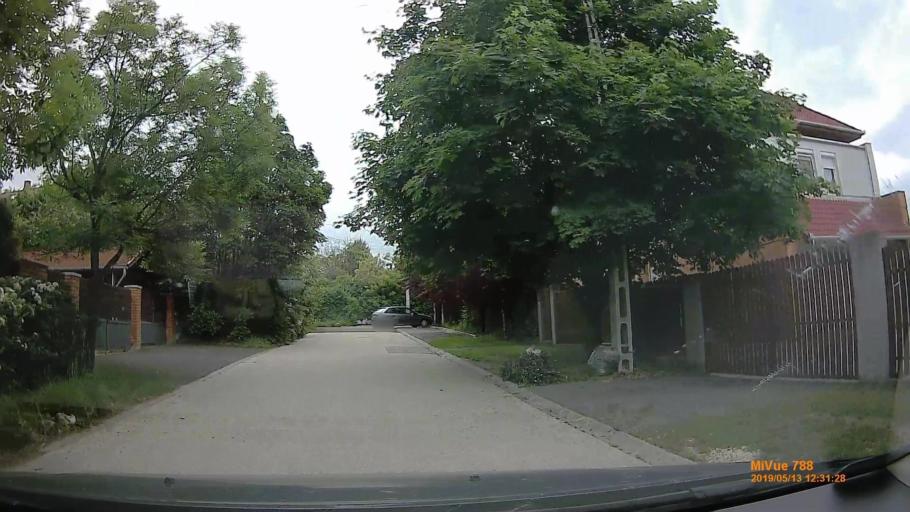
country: HU
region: Pest
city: Diosd
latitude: 47.4064
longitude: 18.9881
